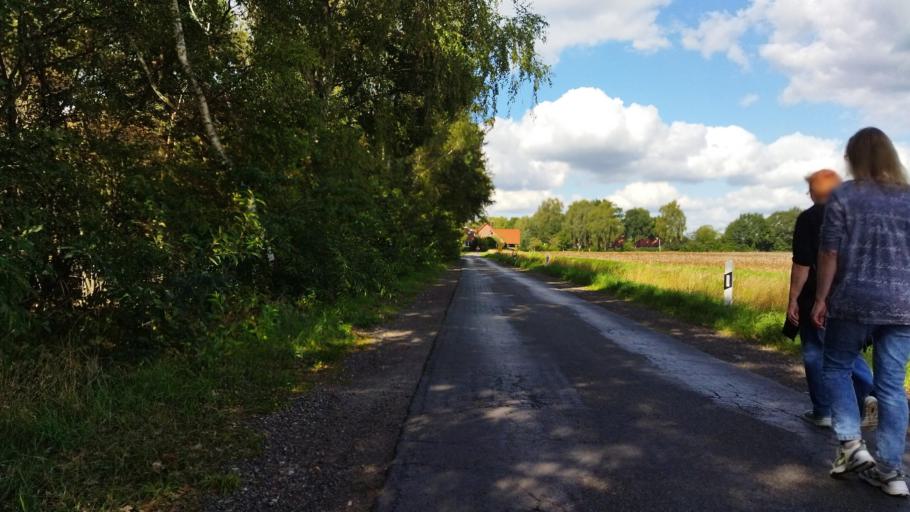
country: DE
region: Lower Saxony
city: Lingen
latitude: 52.4566
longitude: 7.3583
